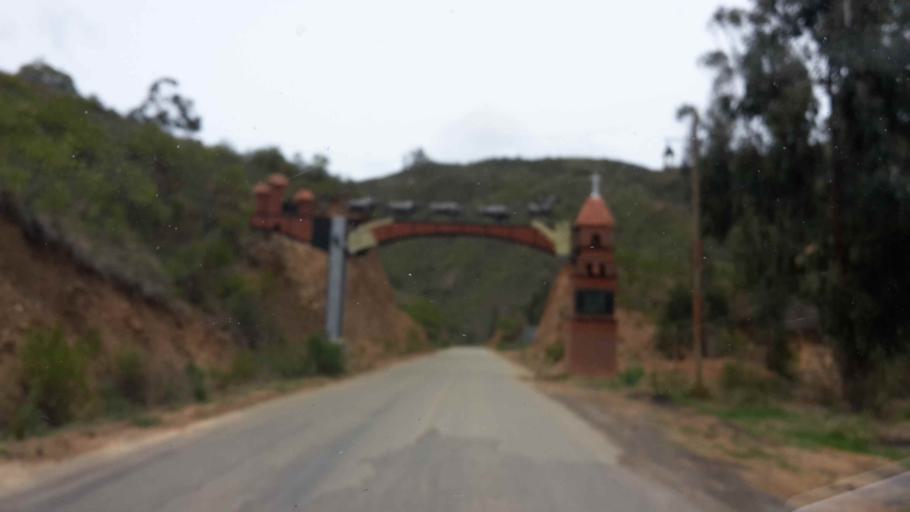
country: BO
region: Cochabamba
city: Totora
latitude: -17.7282
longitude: -65.1922
